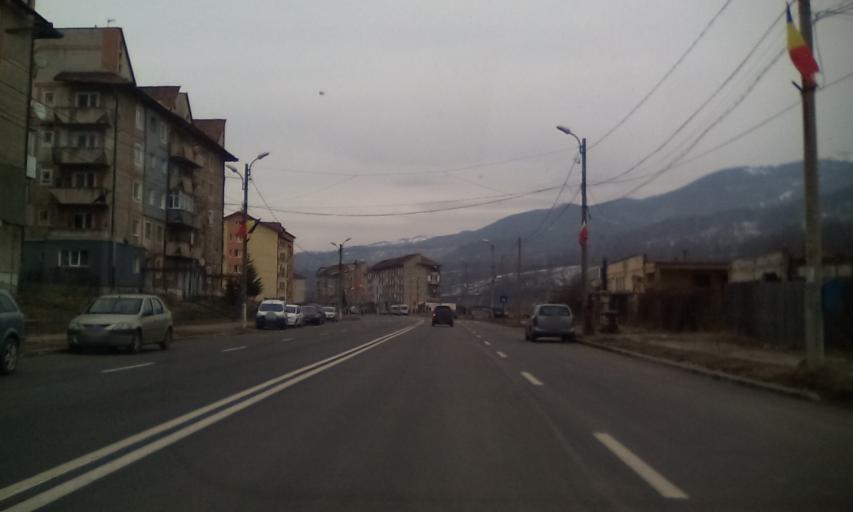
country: RO
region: Hunedoara
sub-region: Comuna Uricani
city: Uricani
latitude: 45.3443
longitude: 23.1828
